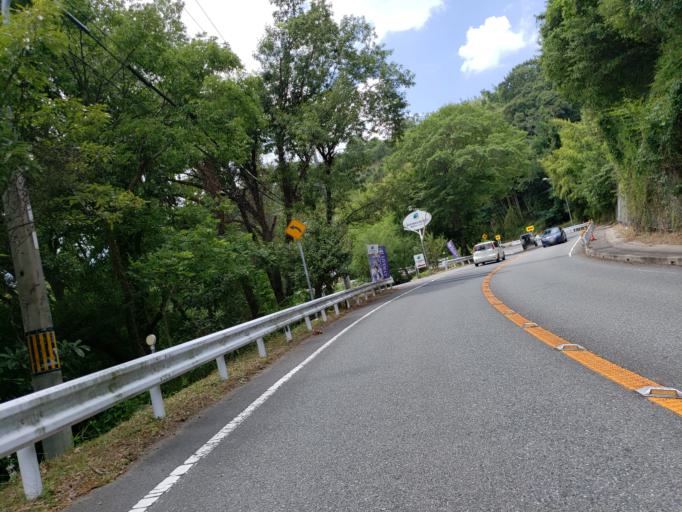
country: JP
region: Hyogo
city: Aioi
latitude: 34.7700
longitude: 134.5134
